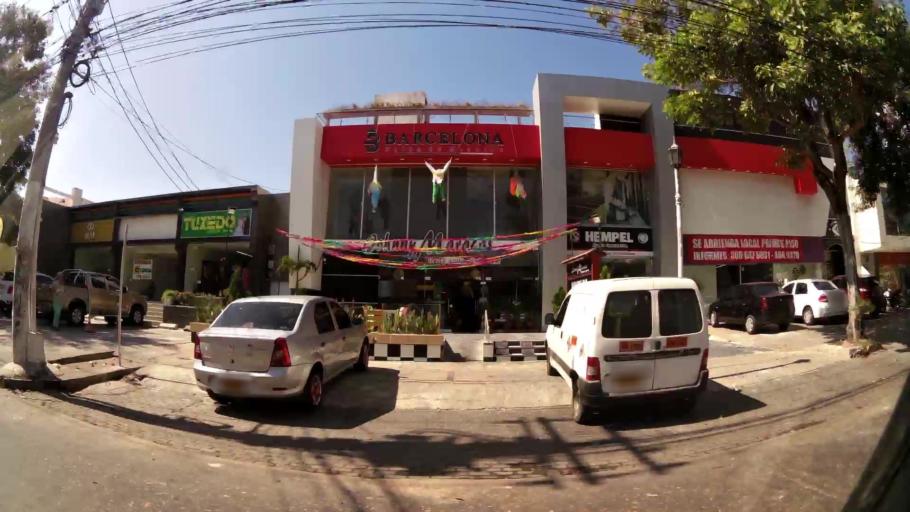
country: CO
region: Atlantico
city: Barranquilla
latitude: 10.9981
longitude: -74.8023
